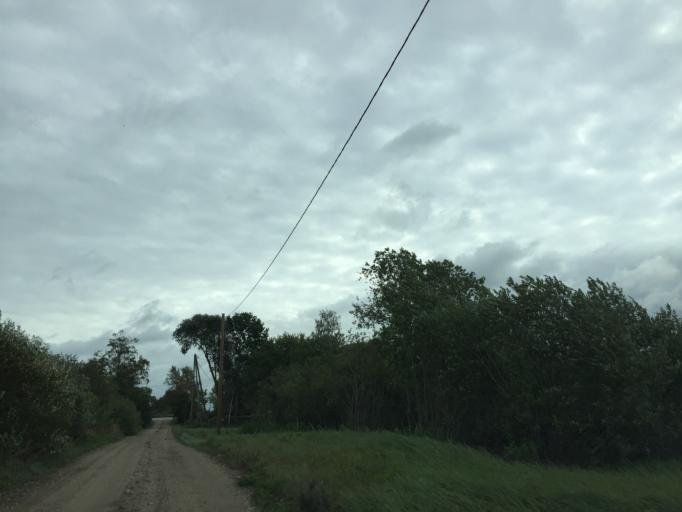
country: LV
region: Salacgrivas
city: Salacgriva
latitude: 57.7367
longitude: 24.3622
